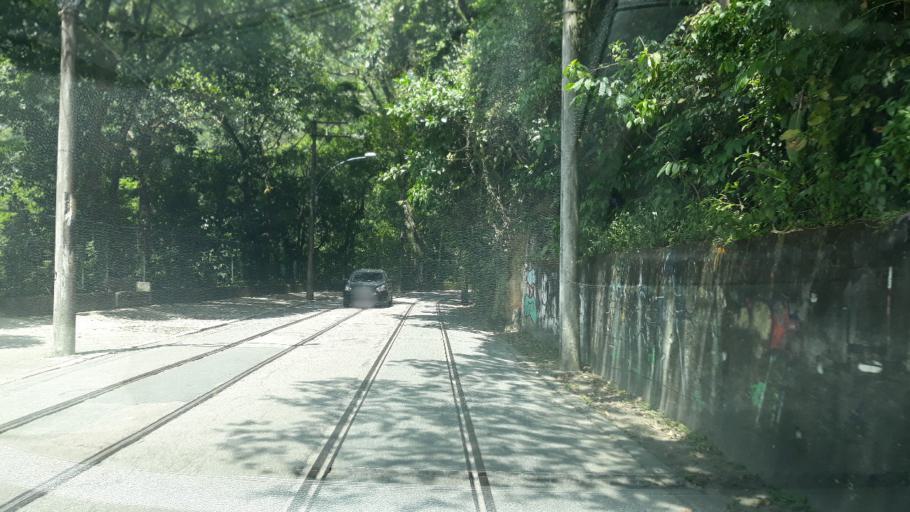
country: BR
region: Rio de Janeiro
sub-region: Rio De Janeiro
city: Rio de Janeiro
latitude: -22.9391
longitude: -43.2089
